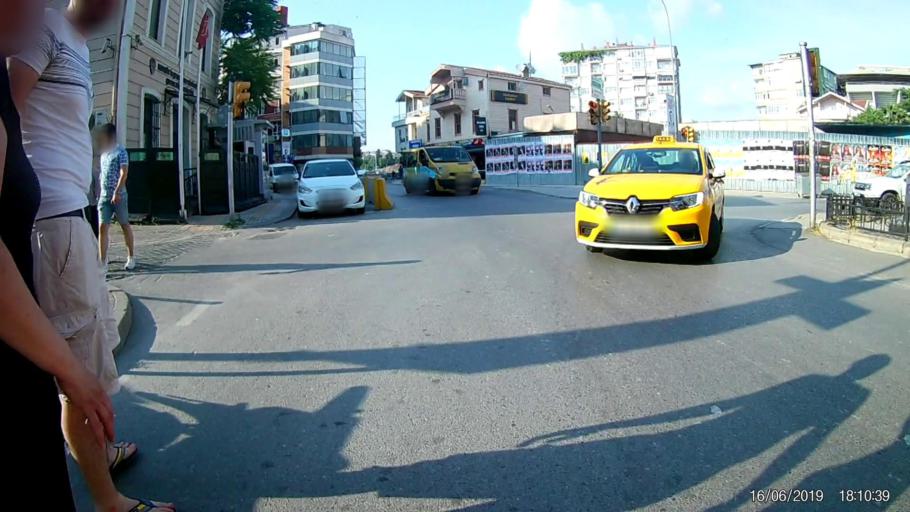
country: TR
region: Istanbul
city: UEskuedar
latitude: 40.9871
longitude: 29.0336
